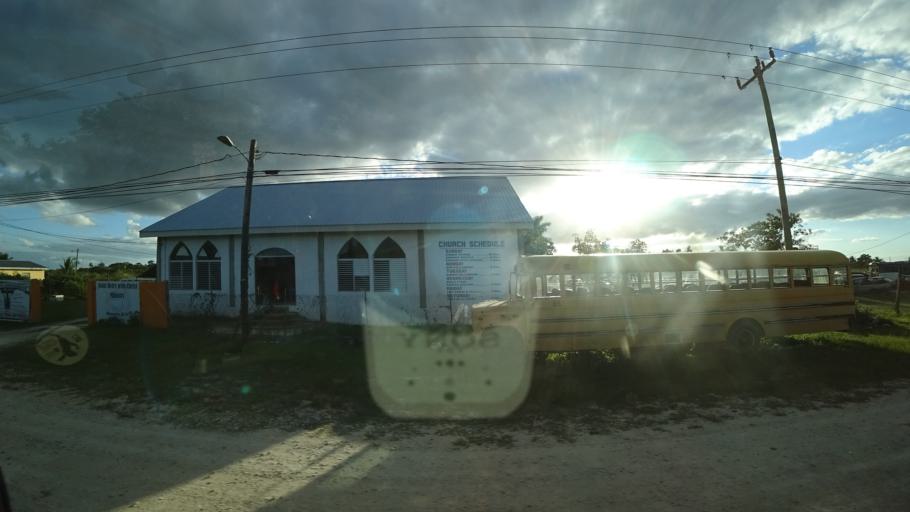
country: BZ
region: Belize
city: Belize City
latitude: 17.5624
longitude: -88.3235
